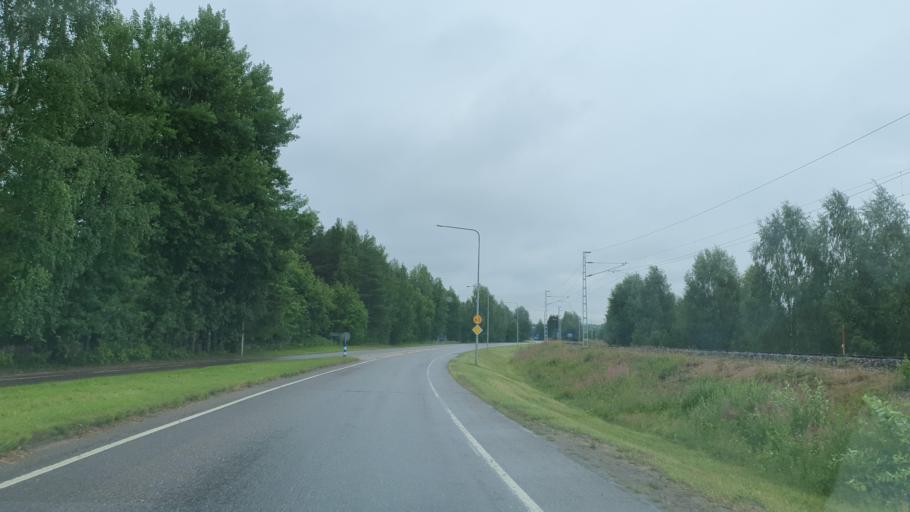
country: FI
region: Lapland
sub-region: Itae-Lappi
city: Kemijaervi
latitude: 66.7157
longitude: 27.4414
